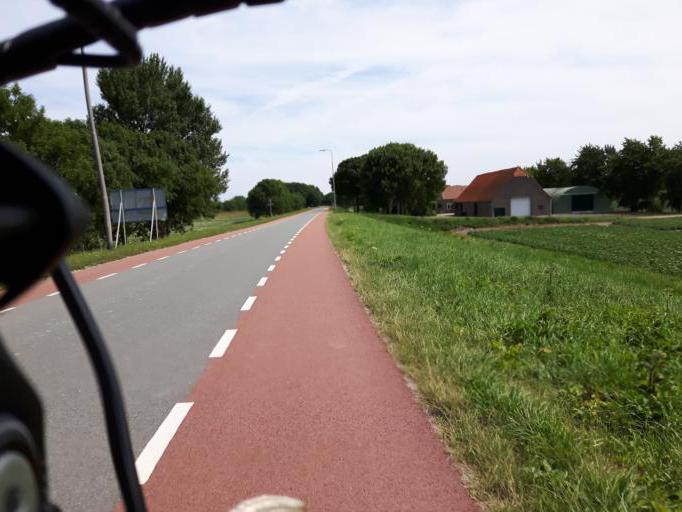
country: NL
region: North Brabant
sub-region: Gemeente Steenbergen
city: Nieuw-Vossemeer
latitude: 51.5863
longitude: 4.2094
